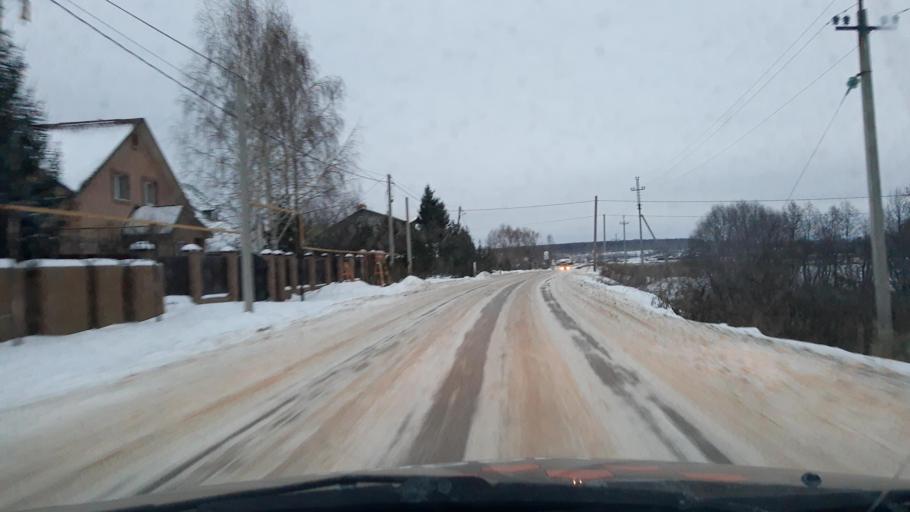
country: RU
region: Bashkortostan
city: Kabakovo
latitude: 54.6499
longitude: 56.1800
